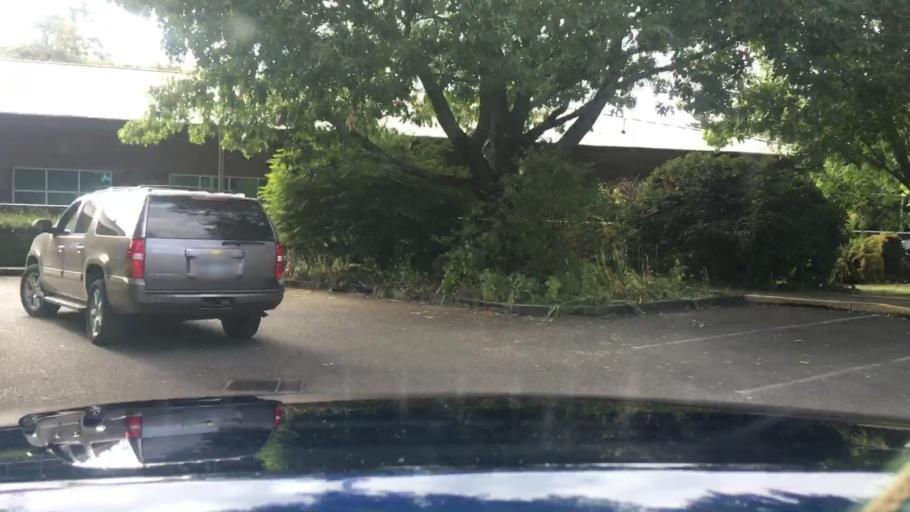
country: US
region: Oregon
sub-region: Lane County
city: Eugene
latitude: 44.0965
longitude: -123.1234
